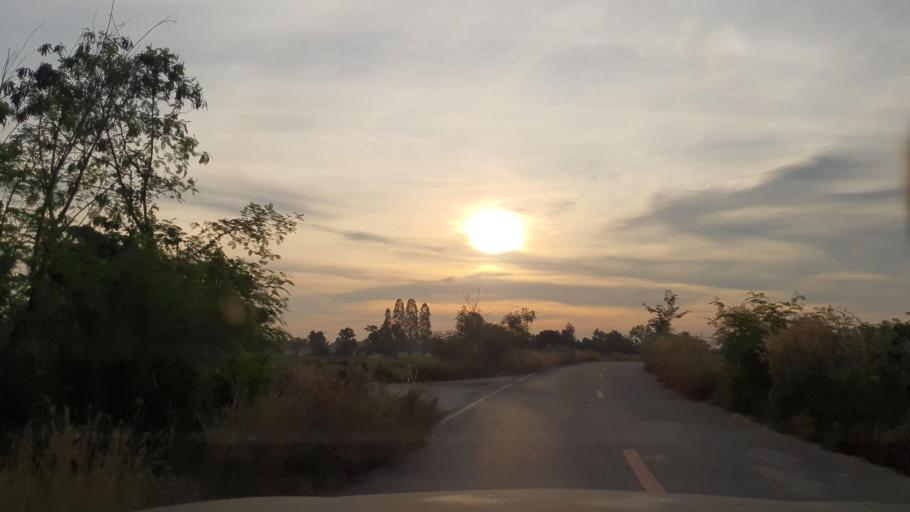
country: TH
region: Uthai Thani
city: Sawang Arom
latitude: 15.7086
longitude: 99.9597
